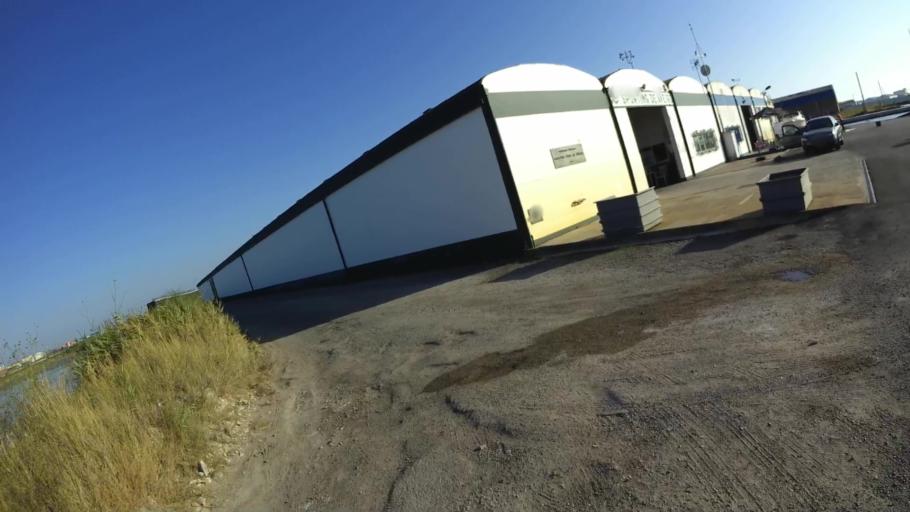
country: PT
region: Aveiro
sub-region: Aveiro
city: Aveiro
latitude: 40.6407
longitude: -8.6719
